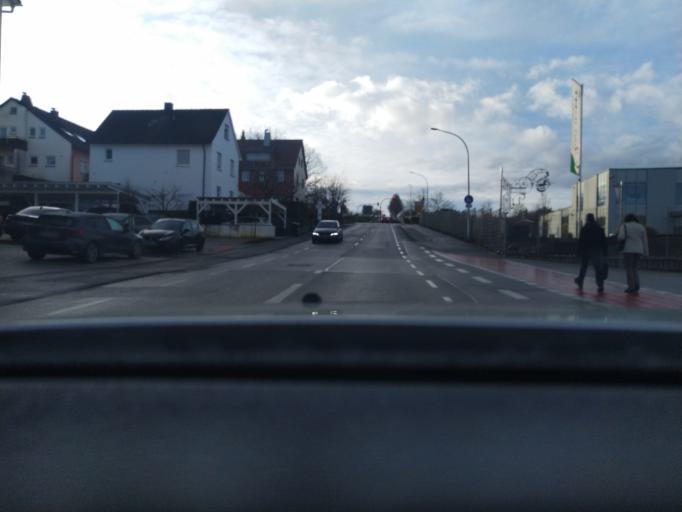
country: DE
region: Baden-Wuerttemberg
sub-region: Regierungsbezirk Stuttgart
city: Backnang
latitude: 48.9379
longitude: 9.4292
